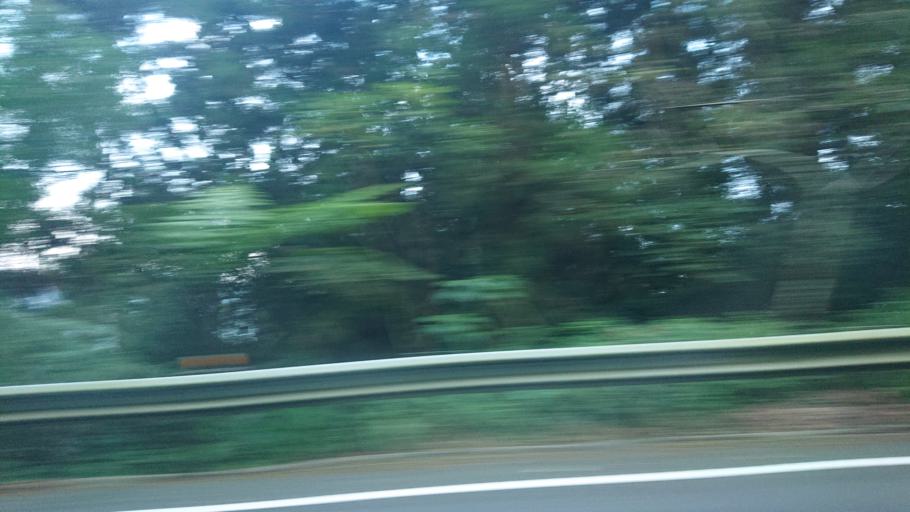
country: TW
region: Taiwan
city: Lugu
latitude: 23.4859
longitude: 120.7458
